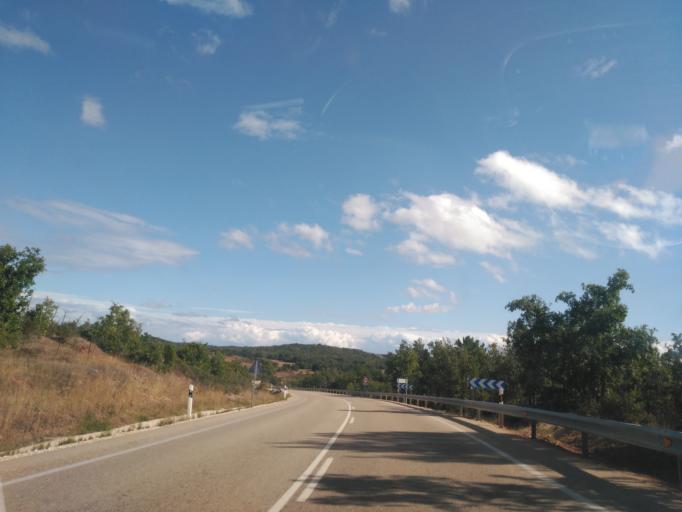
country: ES
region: Castille and Leon
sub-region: Provincia de Burgos
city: Pinilla de los Barruecos
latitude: 41.9403
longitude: -3.2893
